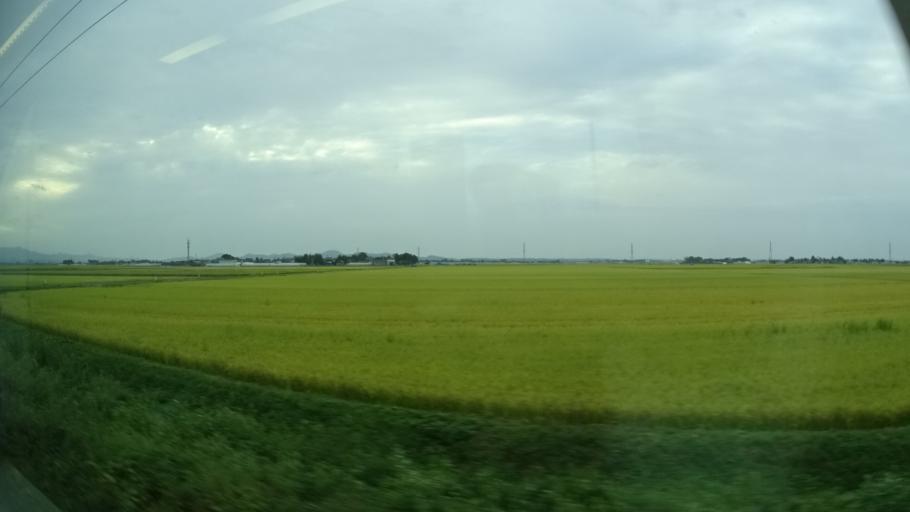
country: JP
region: Yamagata
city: Tsuruoka
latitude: 38.7587
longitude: 139.8830
